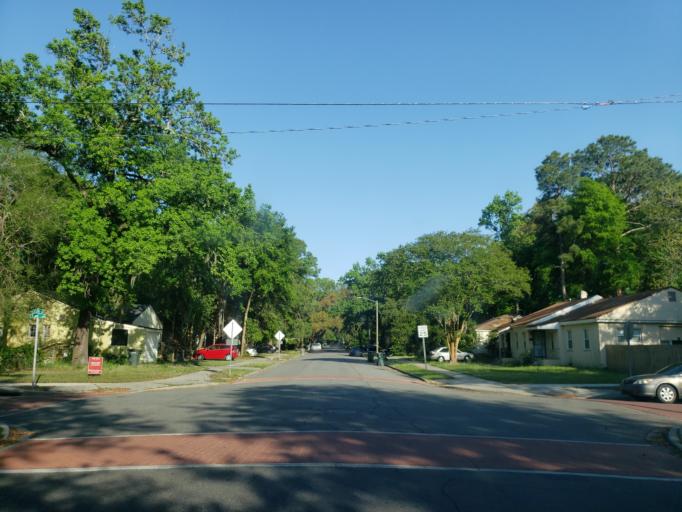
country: US
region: Georgia
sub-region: Chatham County
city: Thunderbolt
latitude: 32.0382
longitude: -81.0852
